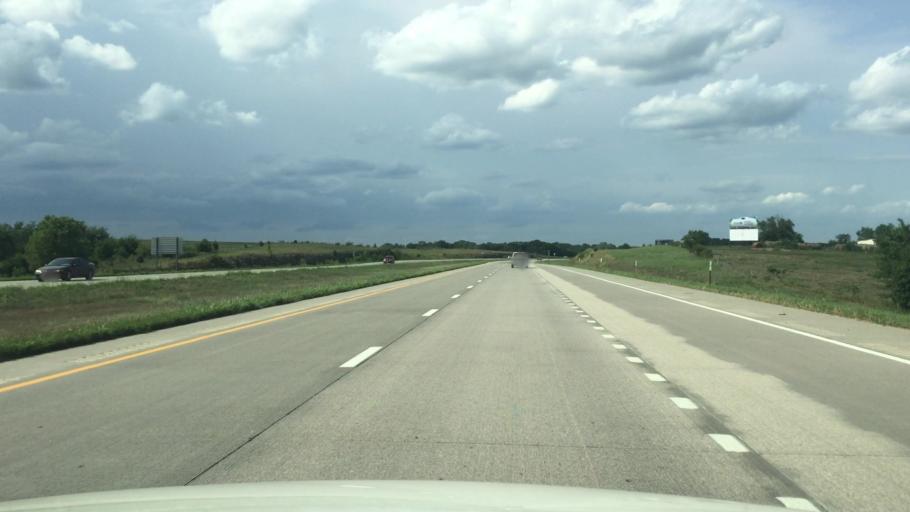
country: US
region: Kansas
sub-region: Miami County
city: Louisburg
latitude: 38.5670
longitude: -94.6949
